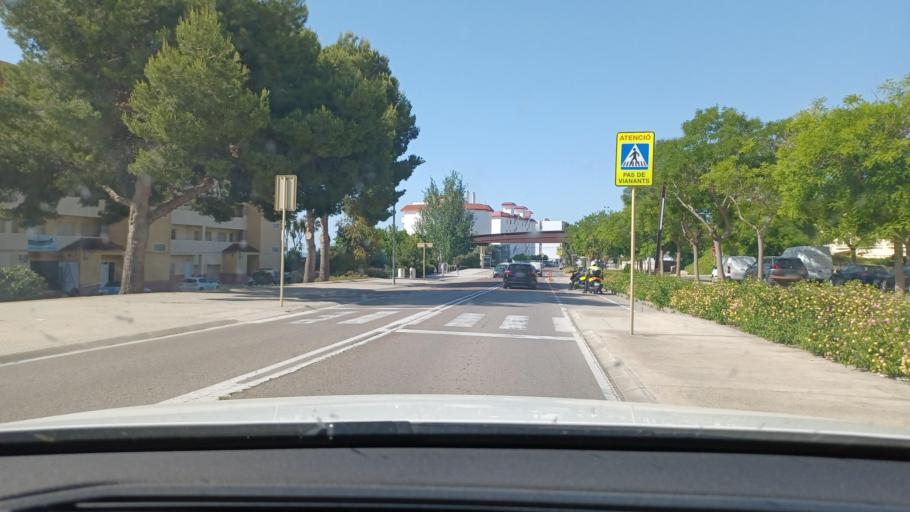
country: ES
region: Catalonia
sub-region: Provincia de Tarragona
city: Sant Carles de la Rapita
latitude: 40.6078
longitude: 0.5832
